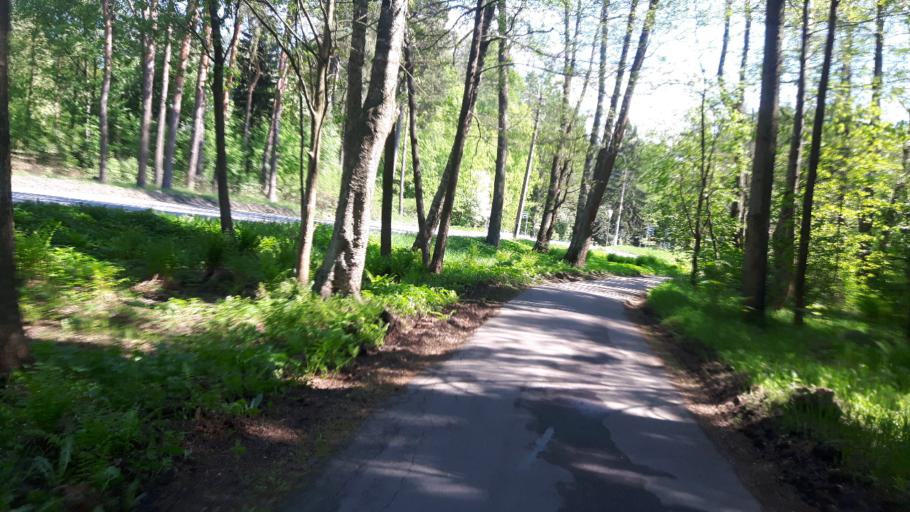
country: RU
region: St.-Petersburg
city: Komarovo
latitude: 60.1667
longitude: 29.8313
